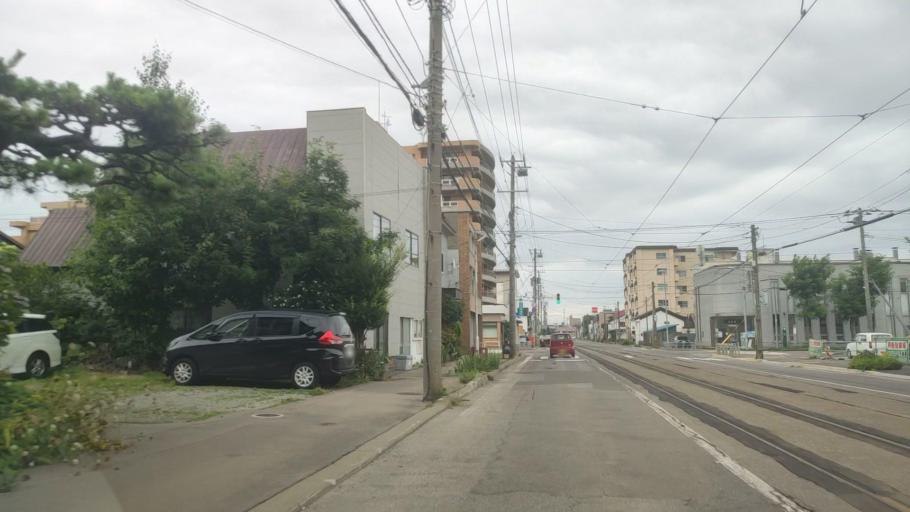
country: JP
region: Hokkaido
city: Hakodate
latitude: 41.7721
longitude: 140.7060
